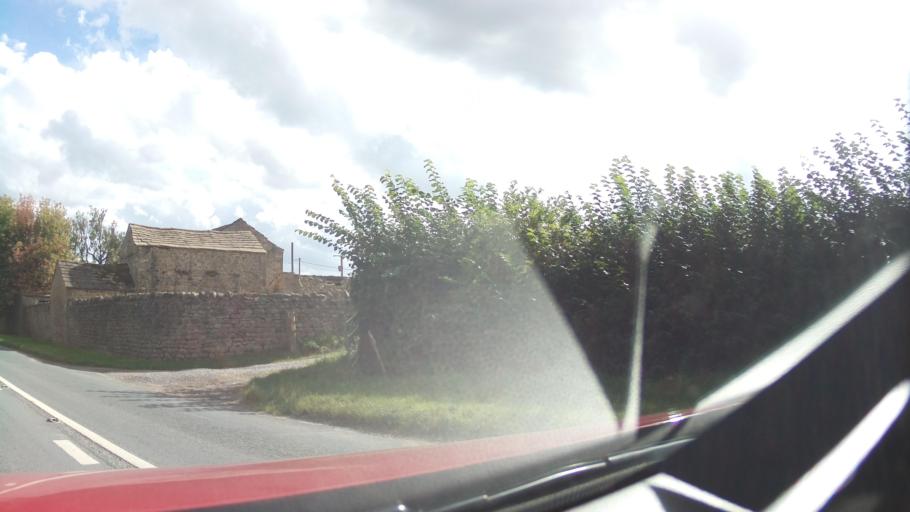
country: GB
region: England
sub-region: North Yorkshire
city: Bedale
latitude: 54.2361
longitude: -1.6749
